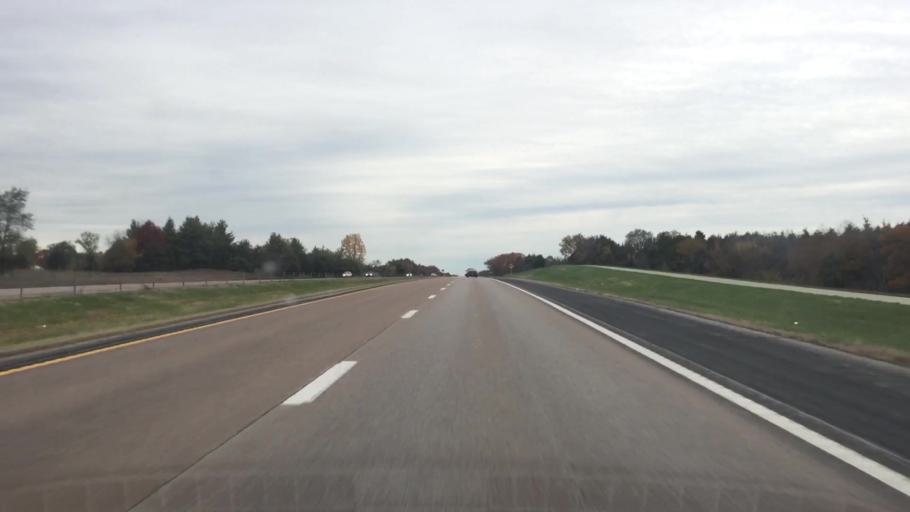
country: US
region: Missouri
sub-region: Boone County
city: Ashland
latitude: 38.7119
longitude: -92.2544
